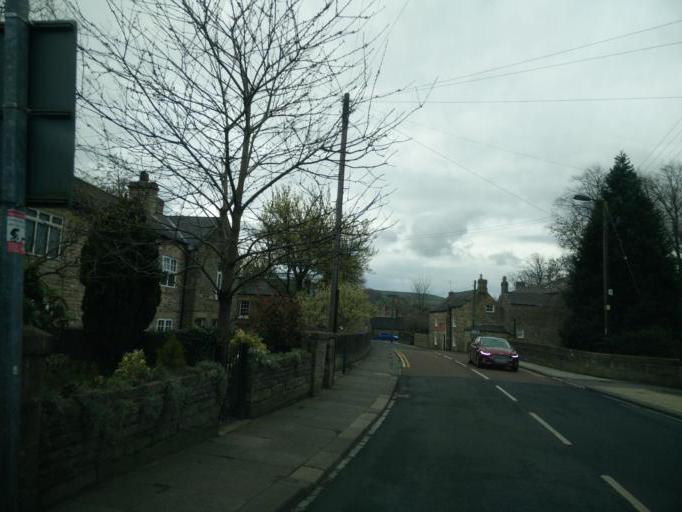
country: GB
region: England
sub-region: County Durham
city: Wolsingham
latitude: 54.7329
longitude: -1.8818
